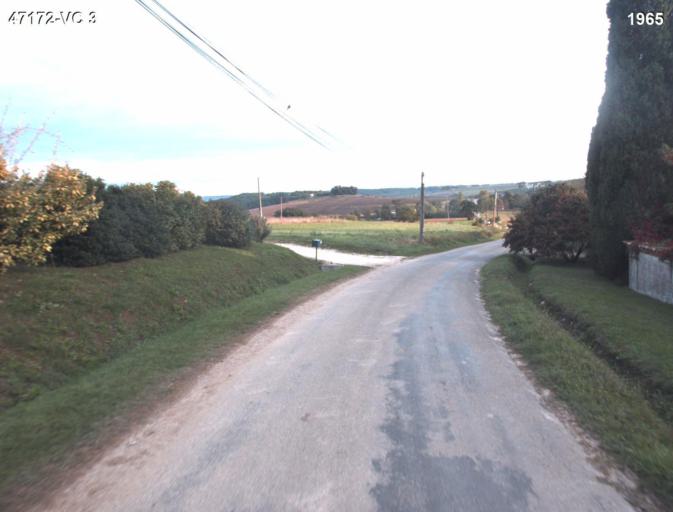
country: FR
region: Aquitaine
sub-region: Departement du Lot-et-Garonne
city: Sainte-Colombe-en-Bruilhois
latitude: 44.1534
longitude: 0.4923
